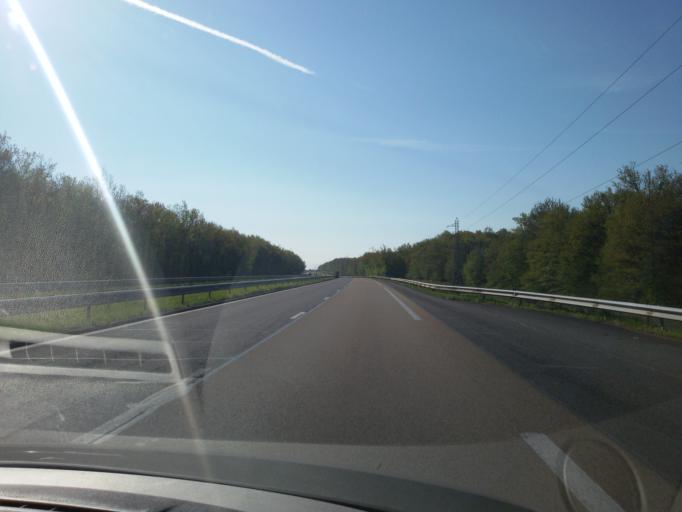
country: FR
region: Centre
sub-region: Departement du Loiret
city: Courtenay
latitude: 48.0839
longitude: 3.0470
